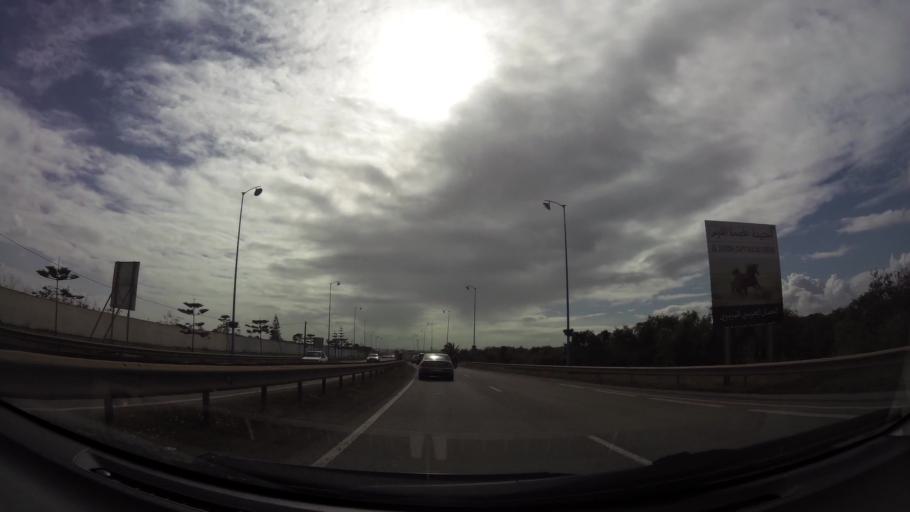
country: MA
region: Doukkala-Abda
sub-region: El-Jadida
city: El Jadida
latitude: 33.2464
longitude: -8.4568
